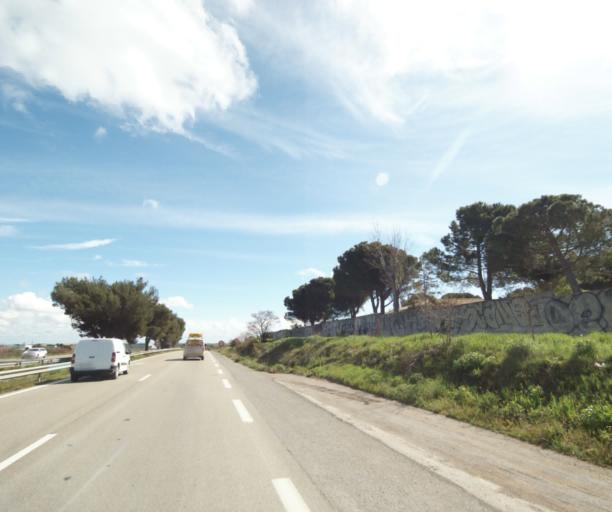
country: FR
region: Languedoc-Roussillon
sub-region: Departement de l'Herault
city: Saint-Jean-de-Vedas
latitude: 43.5522
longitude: 3.8371
